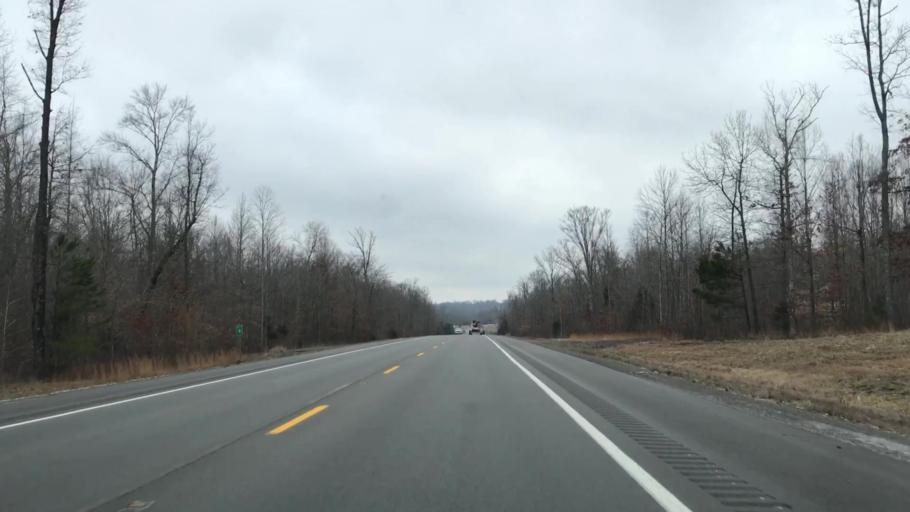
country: US
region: Kentucky
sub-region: Adair County
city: Columbia
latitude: 37.0463
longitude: -85.3660
